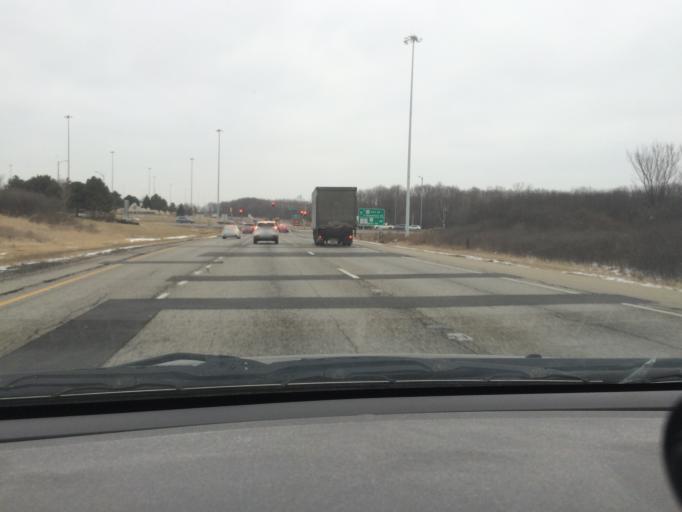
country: US
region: Illinois
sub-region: Cook County
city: Hoffman Estates
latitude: 42.0350
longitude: -88.0298
